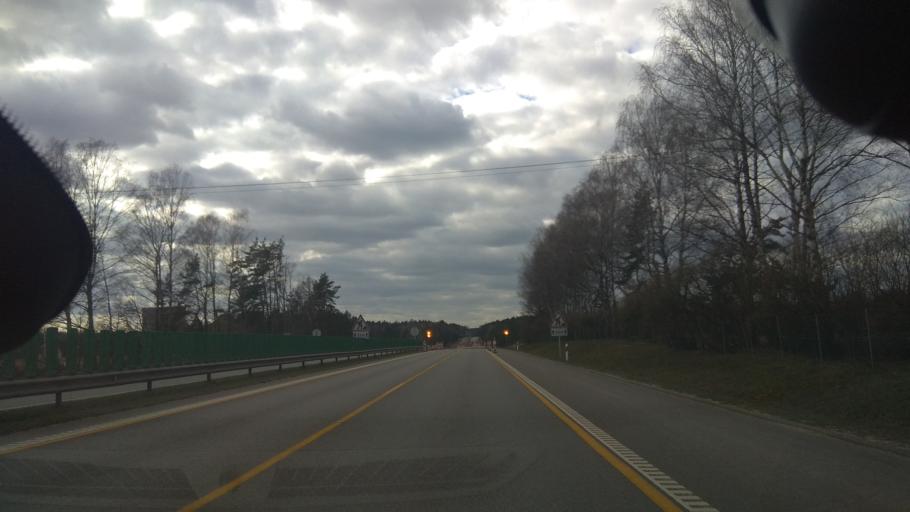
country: LT
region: Vilnius County
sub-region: Vilniaus Rajonas
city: Vievis
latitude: 54.7551
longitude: 24.8991
